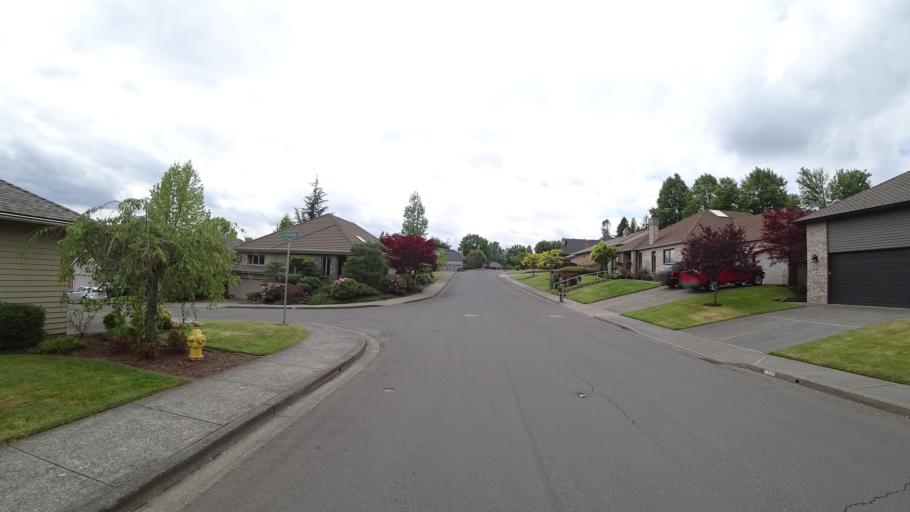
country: US
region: Oregon
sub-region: Washington County
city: Garden Home-Whitford
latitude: 45.4734
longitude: -122.7512
